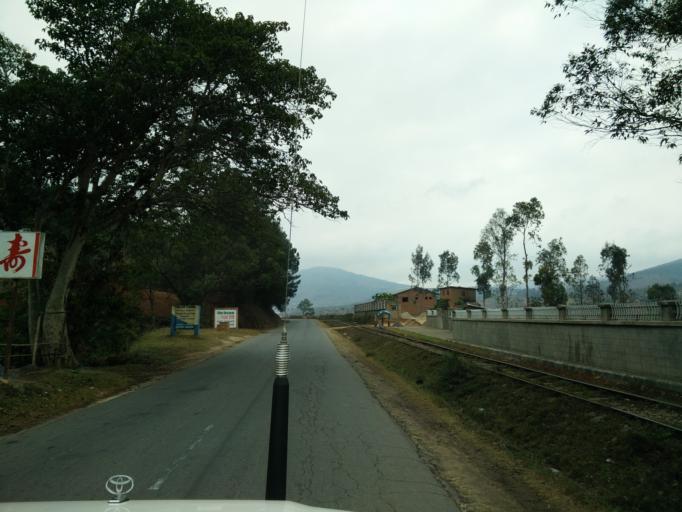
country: MG
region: Upper Matsiatra
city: Fianarantsoa
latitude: -21.4307
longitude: 47.1339
